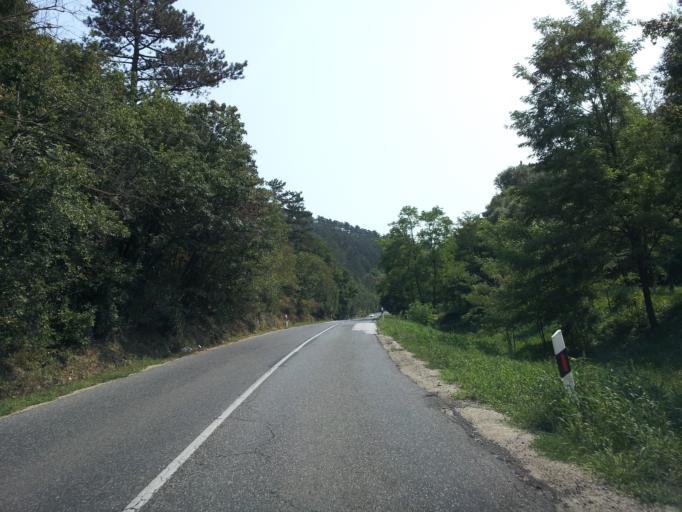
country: HU
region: Veszprem
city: Csopak
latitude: 46.9888
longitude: 17.9173
